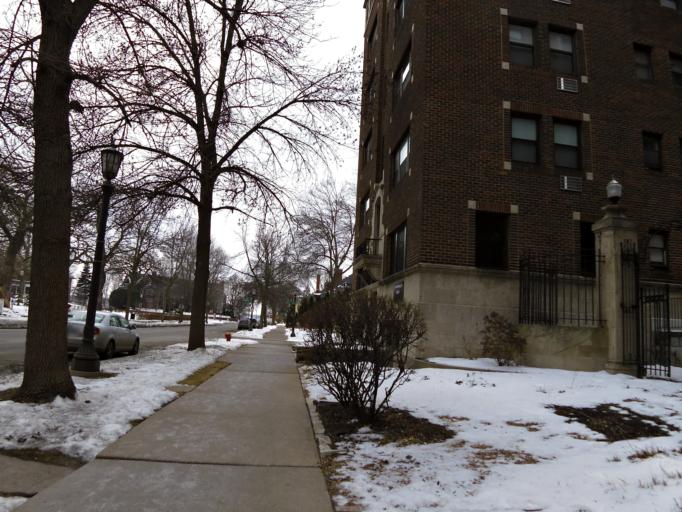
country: US
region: Minnesota
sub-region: Ramsey County
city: Saint Paul
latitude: 44.9438
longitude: -93.1162
